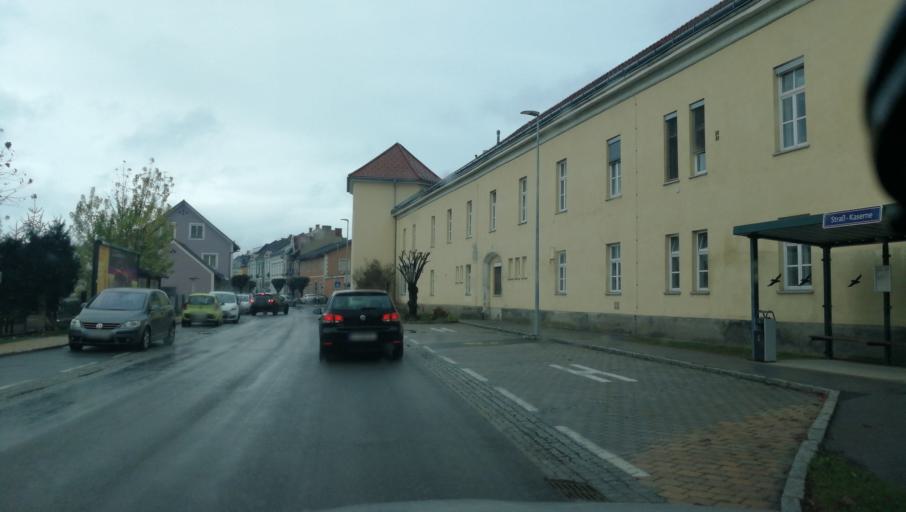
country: AT
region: Styria
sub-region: Politischer Bezirk Leibnitz
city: Strass in Steiermark
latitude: 46.7273
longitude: 15.6254
